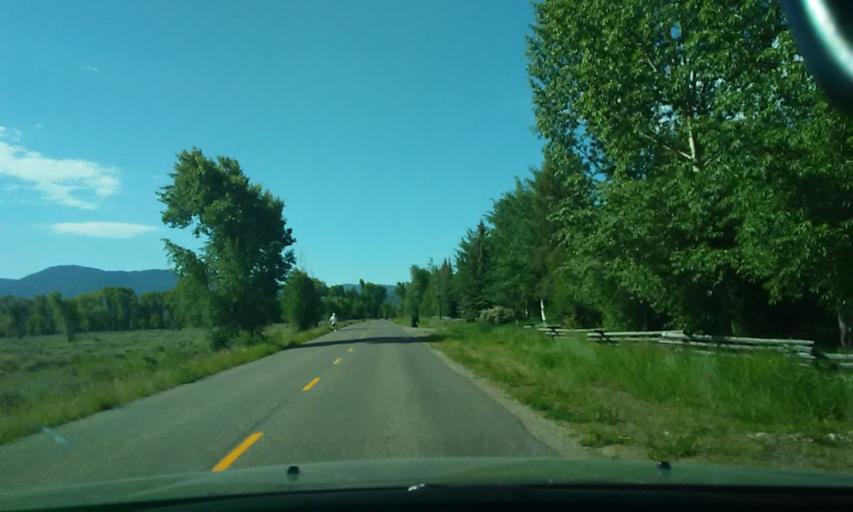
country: US
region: Wyoming
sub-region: Teton County
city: Jackson
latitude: 43.5716
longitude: -110.7435
